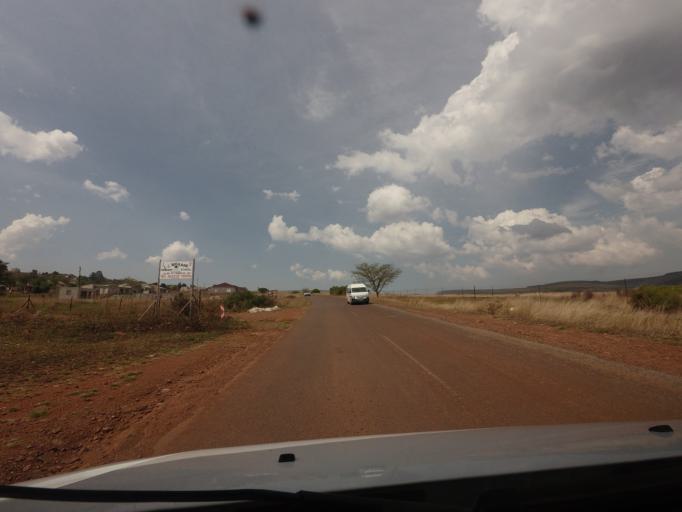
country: ZA
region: Mpumalanga
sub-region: Ehlanzeni District
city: Graksop
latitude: -24.6644
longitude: 30.8131
